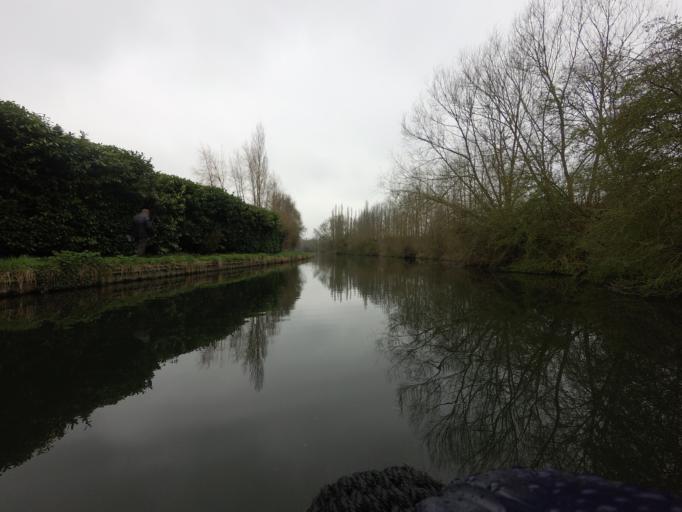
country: GB
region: England
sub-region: Hertfordshire
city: Kings Langley
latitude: 51.7229
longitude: -0.4499
